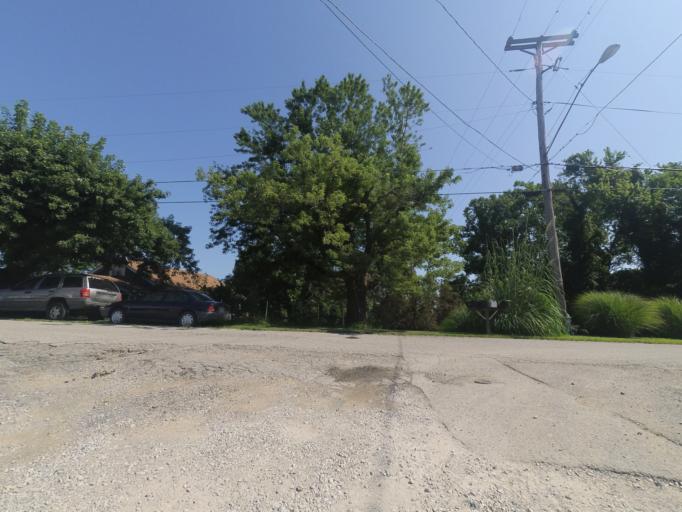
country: US
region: West Virginia
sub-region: Cabell County
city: Huntington
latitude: 38.4368
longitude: -82.4385
